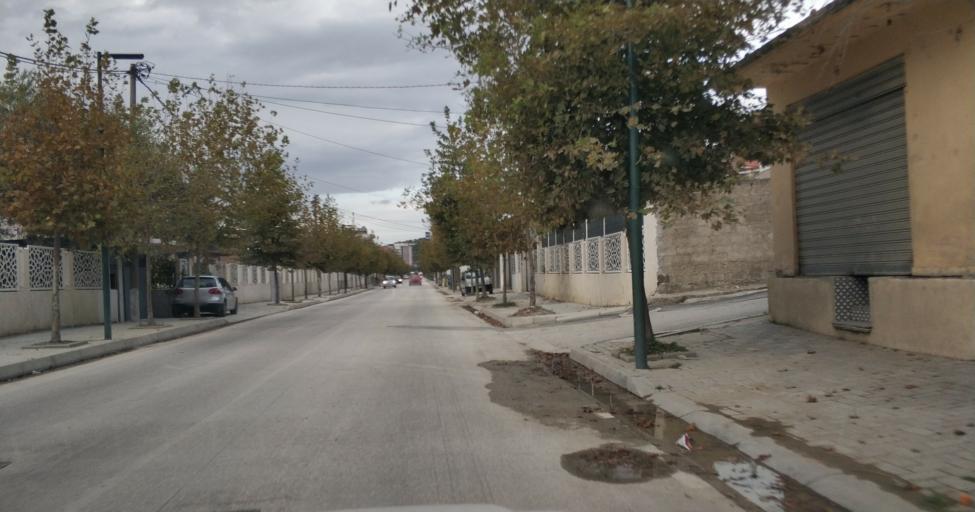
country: AL
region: Vlore
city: Vlore
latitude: 40.4495
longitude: 19.4970
